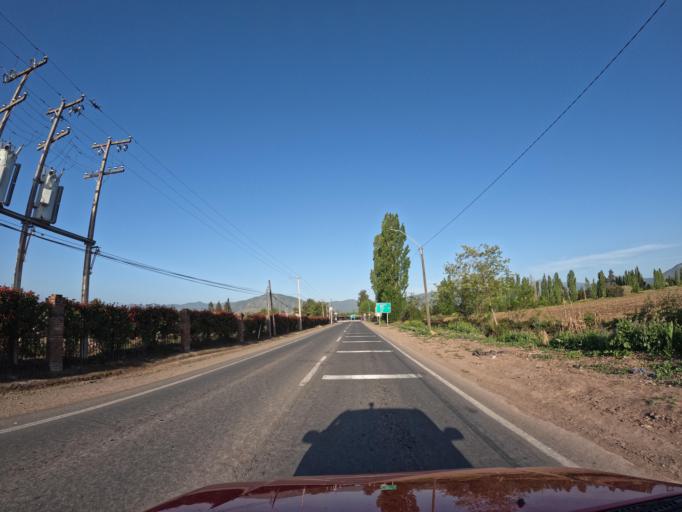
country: CL
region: O'Higgins
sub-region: Provincia de Colchagua
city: Santa Cruz
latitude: -34.5211
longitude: -71.3663
